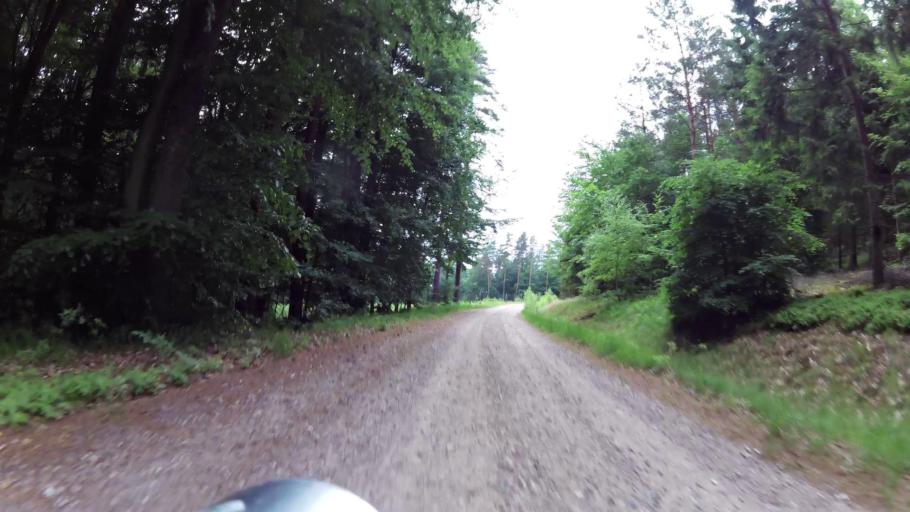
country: PL
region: West Pomeranian Voivodeship
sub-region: Powiat szczecinecki
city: Bialy Bor
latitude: 53.9348
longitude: 16.8289
